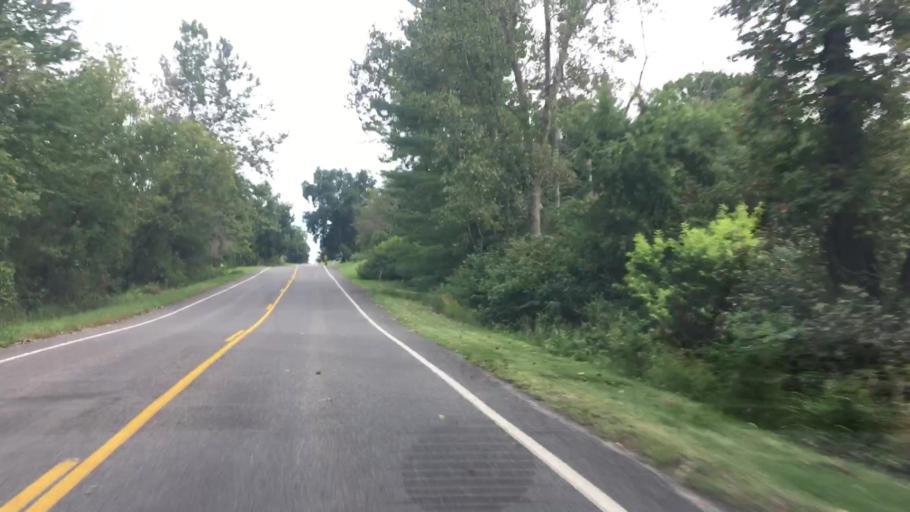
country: US
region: Michigan
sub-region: Kent County
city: Byron Center
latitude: 42.8364
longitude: -85.7825
